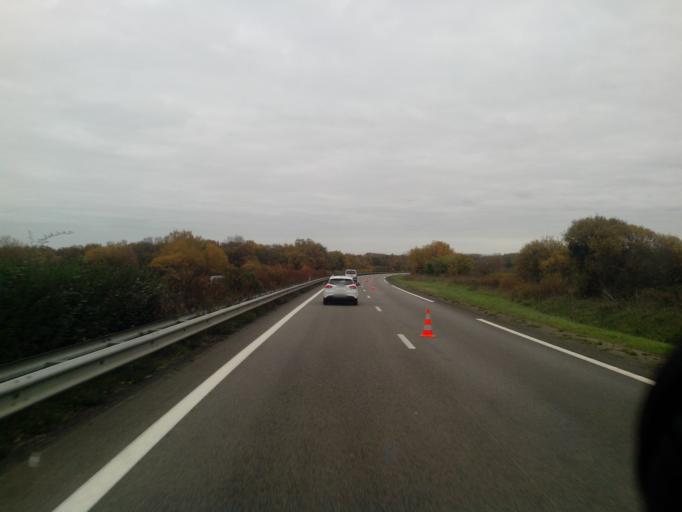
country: FR
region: Pays de la Loire
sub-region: Departement de la Loire-Atlantique
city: La Haie-Fouassiere
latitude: 47.1710
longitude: -1.3826
